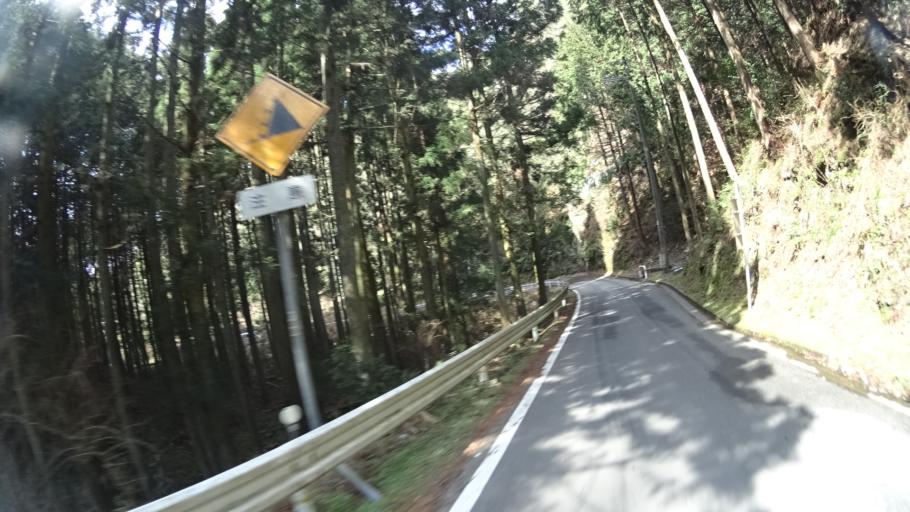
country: JP
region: Kyoto
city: Uji
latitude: 34.8245
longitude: 135.8875
